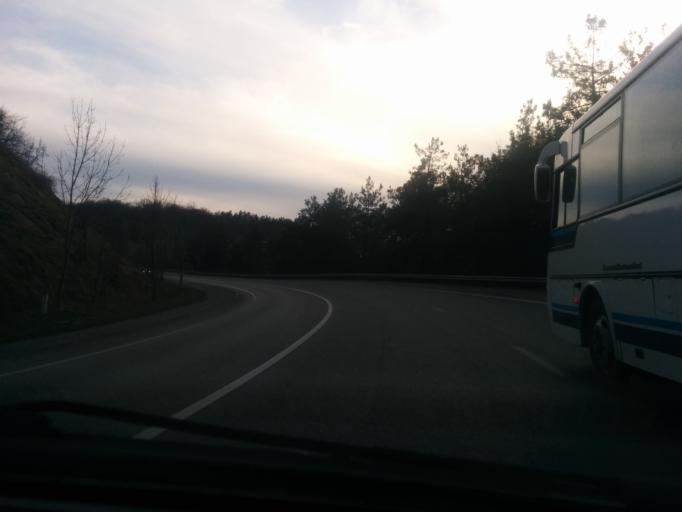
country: RU
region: Krasnodarskiy
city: Ol'ginka
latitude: 44.1937
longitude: 38.8898
